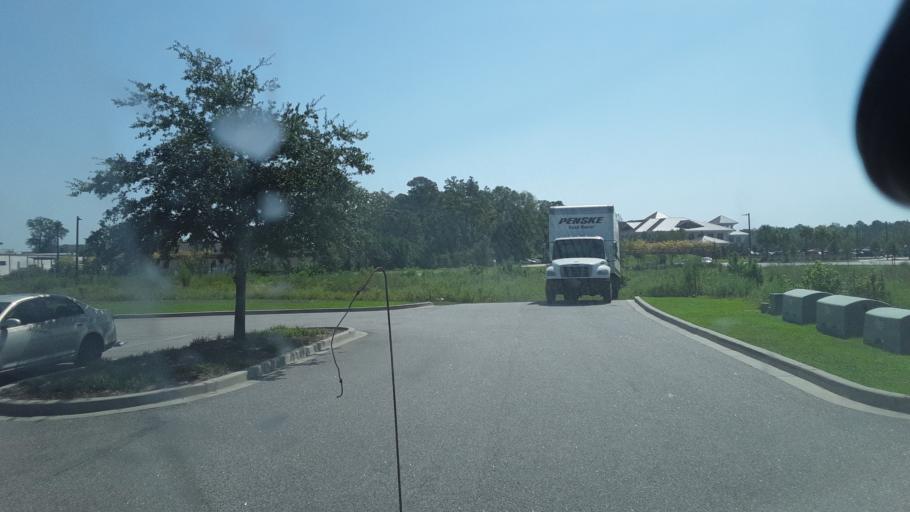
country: US
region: South Carolina
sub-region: Horry County
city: Myrtle Beach
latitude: 33.7588
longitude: -78.8554
